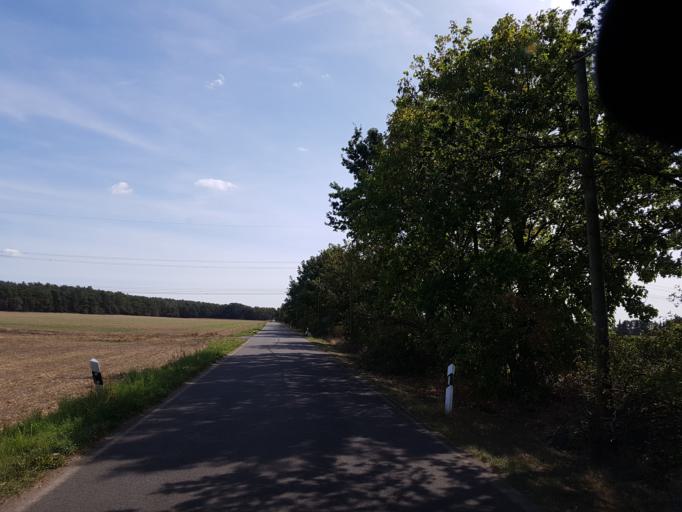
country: DE
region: Brandenburg
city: Luckau
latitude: 51.8628
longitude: 13.6496
